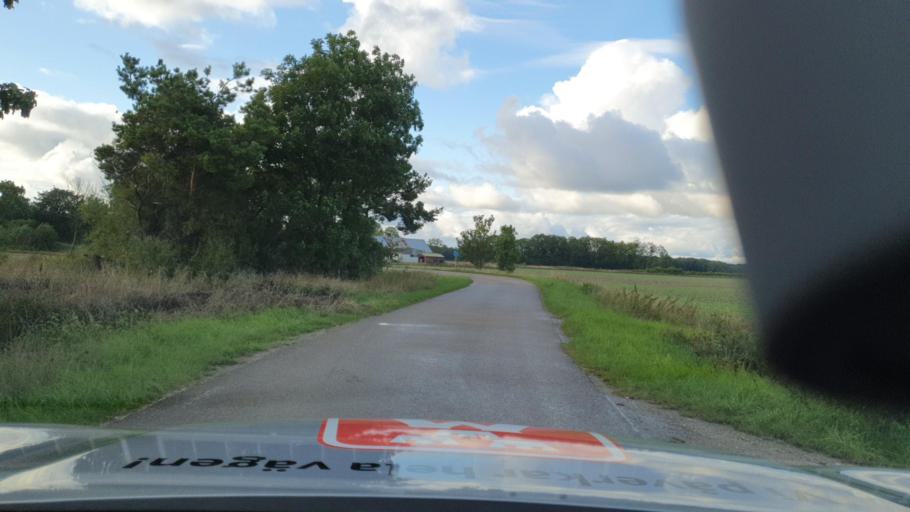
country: SE
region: Gotland
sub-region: Gotland
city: Hemse
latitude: 57.2013
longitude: 18.2502
